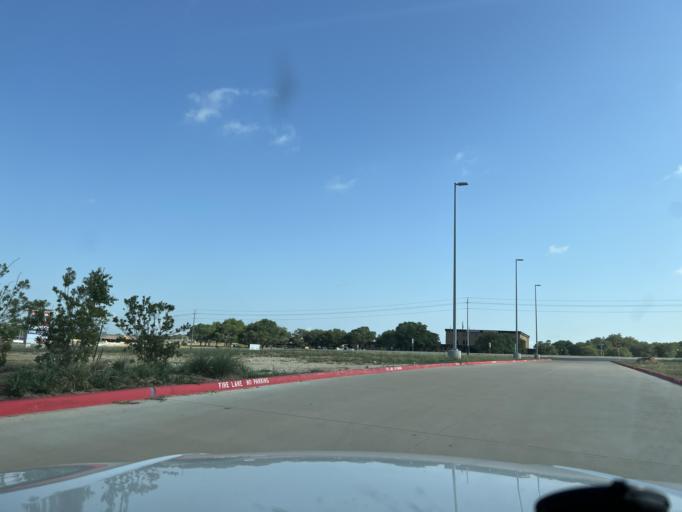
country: US
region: Texas
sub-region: Washington County
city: Brenham
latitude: 30.1412
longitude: -96.3851
